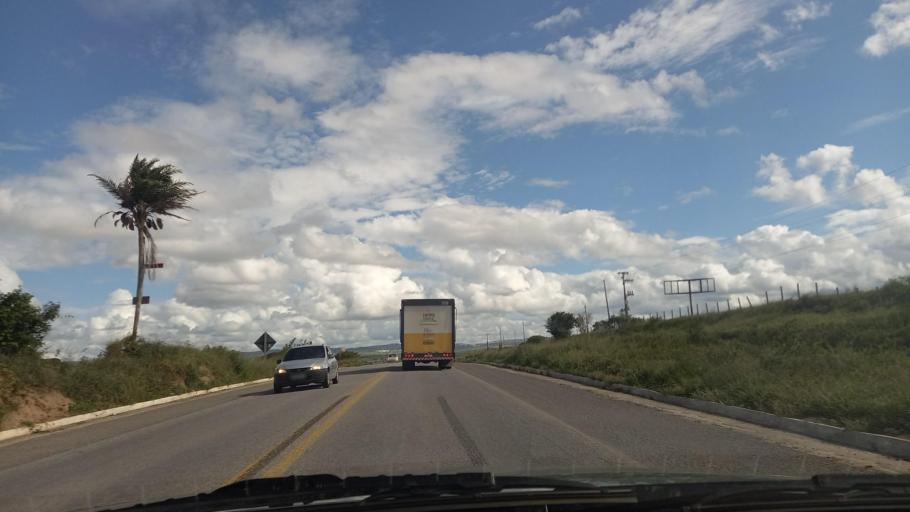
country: BR
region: Pernambuco
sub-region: Sao Joao
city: Sao Joao
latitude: -8.7750
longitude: -36.4276
